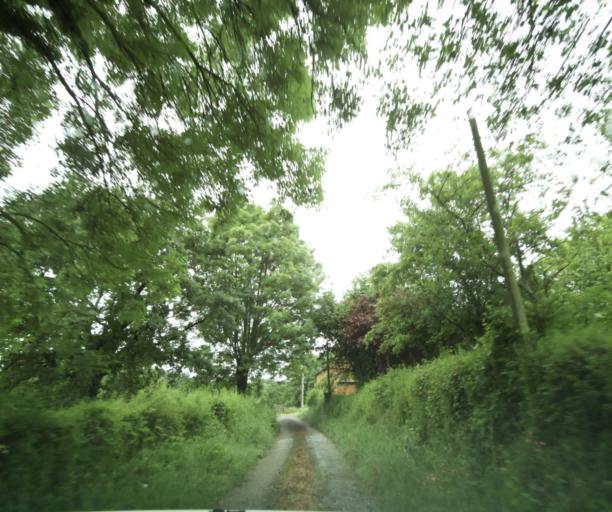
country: FR
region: Bourgogne
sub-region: Departement de Saone-et-Loire
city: La Clayette
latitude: 46.3472
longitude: 4.2121
